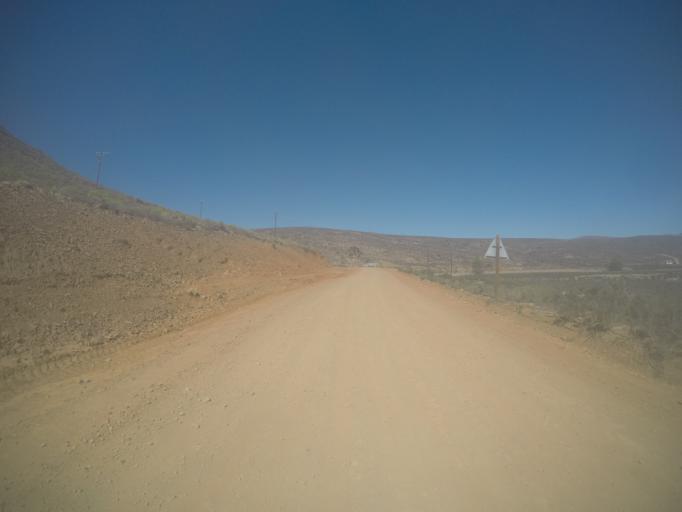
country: ZA
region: Western Cape
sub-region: West Coast District Municipality
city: Clanwilliam
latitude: -32.5004
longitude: 19.3386
